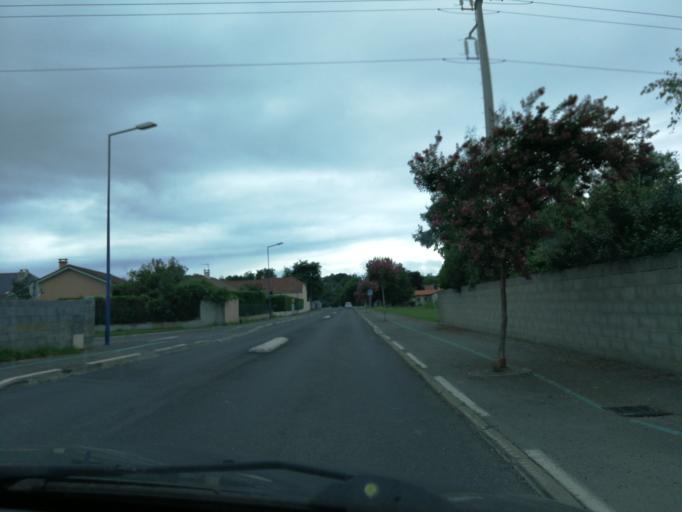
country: FR
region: Midi-Pyrenees
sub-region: Departement des Hautes-Pyrenees
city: Bazet
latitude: 43.2762
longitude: 0.0876
